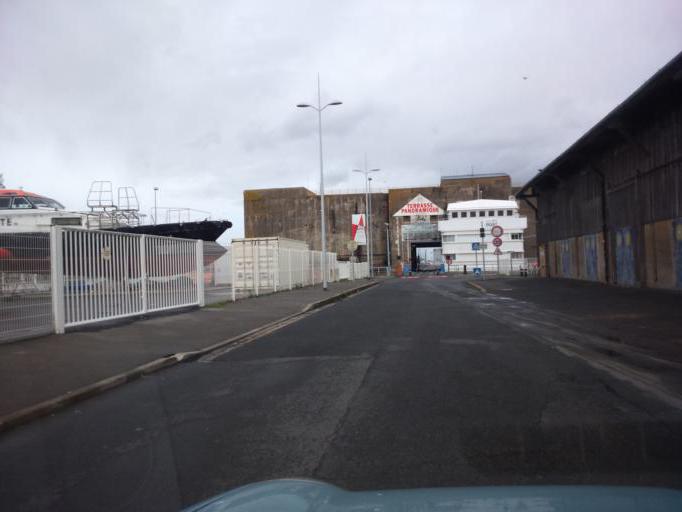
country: FR
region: Pays de la Loire
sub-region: Departement de la Loire-Atlantique
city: Saint-Nazaire
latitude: 47.2745
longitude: -2.1996
